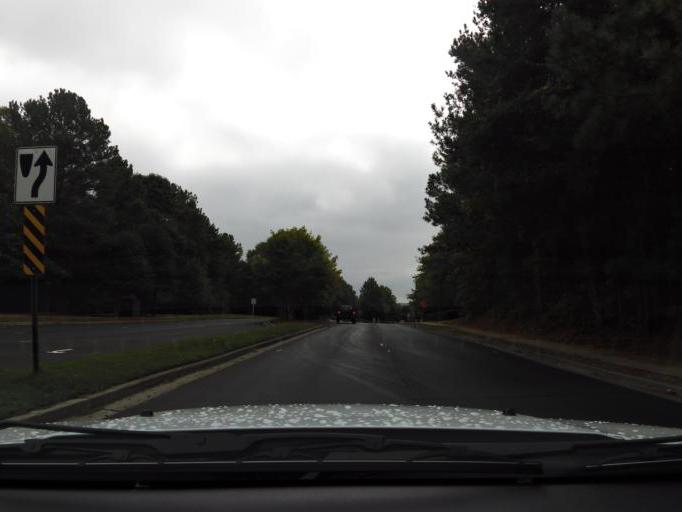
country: US
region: Georgia
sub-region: Cobb County
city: Kennesaw
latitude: 34.0437
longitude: -84.5754
